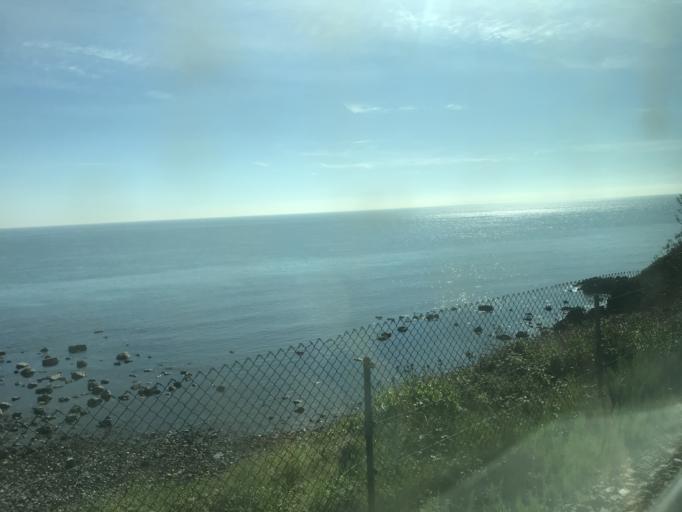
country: IE
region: Leinster
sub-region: Wicklow
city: Bray
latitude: 53.1946
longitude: -6.0855
